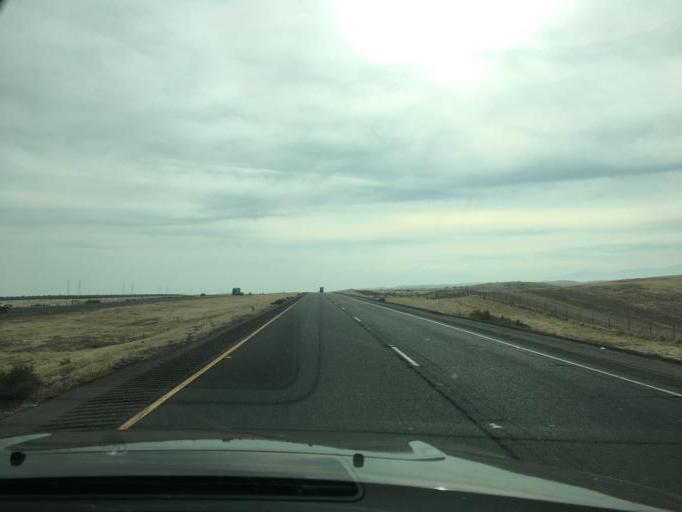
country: US
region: California
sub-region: Fresno County
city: Mendota
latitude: 36.5146
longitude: -120.4686
